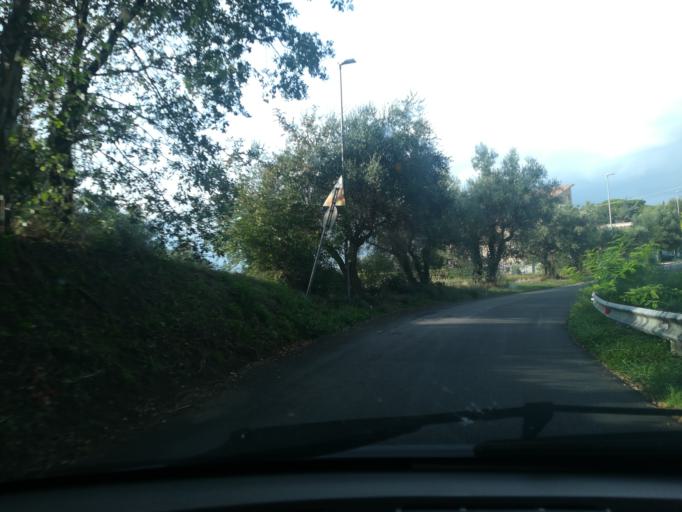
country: IT
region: The Marches
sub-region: Provincia di Macerata
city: Macerata
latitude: 43.3058
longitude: 13.4526
